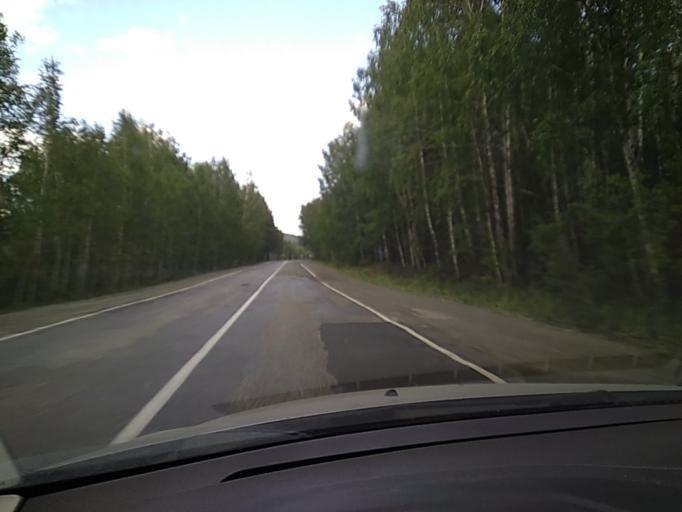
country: RU
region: Chelyabinsk
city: Karabash
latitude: 55.5022
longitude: 60.2655
